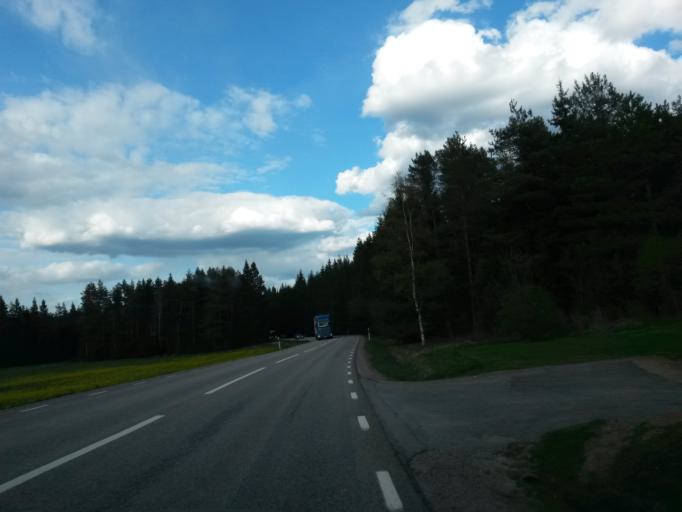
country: SE
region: Vaestra Goetaland
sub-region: Tranemo Kommun
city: Langhem
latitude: 57.6022
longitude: 13.1321
